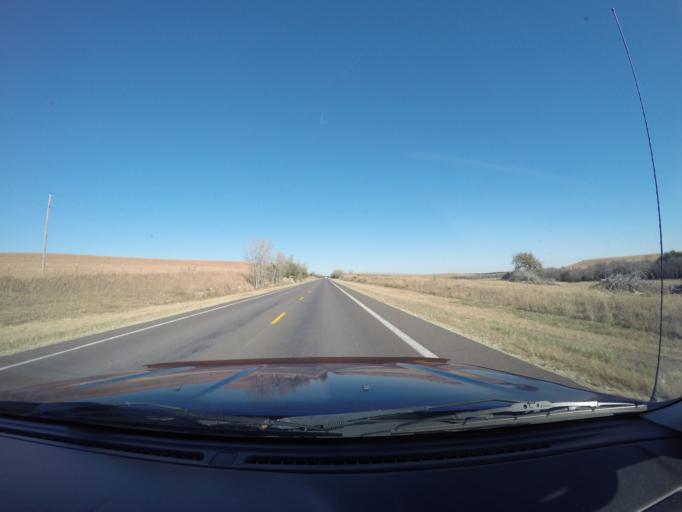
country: US
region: Kansas
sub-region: Marshall County
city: Blue Rapids
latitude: 39.4421
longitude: -96.7643
